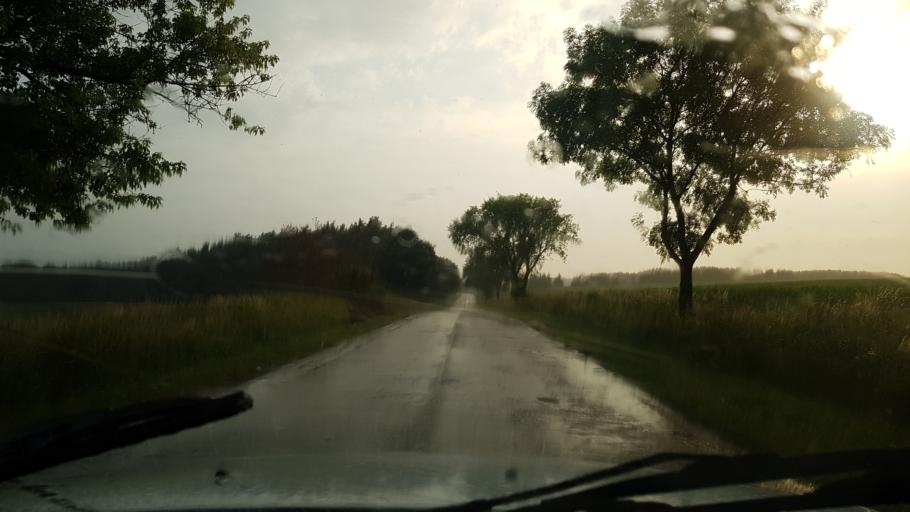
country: PL
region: West Pomeranian Voivodeship
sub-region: Powiat lobeski
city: Lobez
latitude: 53.6418
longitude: 15.6625
